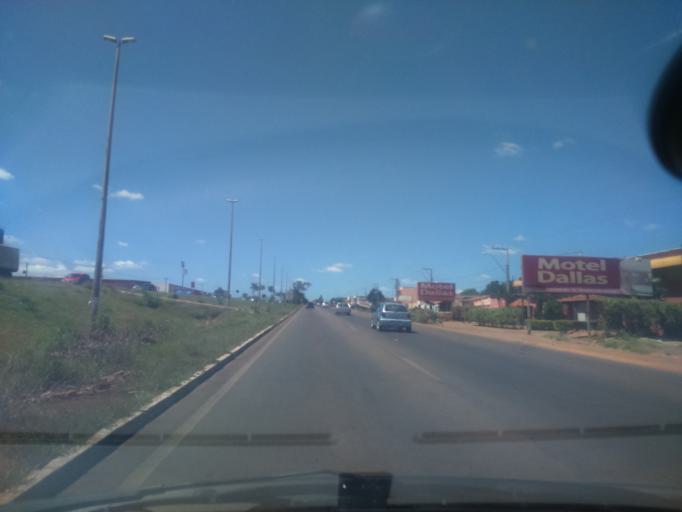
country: BR
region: Goias
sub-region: Luziania
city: Luziania
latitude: -16.0495
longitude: -48.0007
